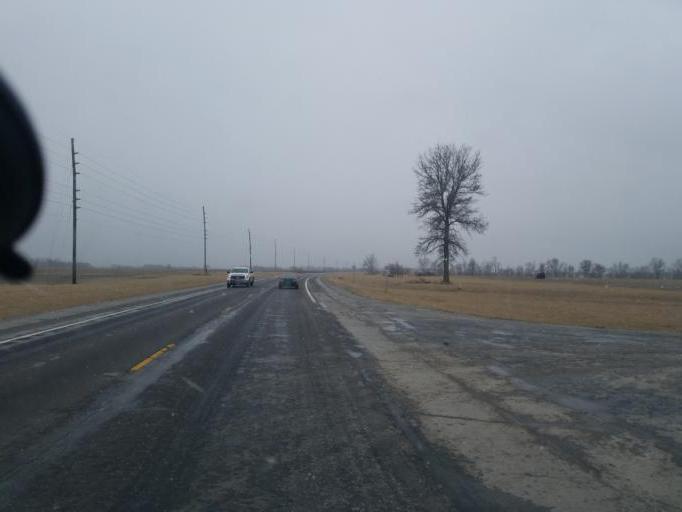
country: US
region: Missouri
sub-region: Schuyler County
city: Lancaster
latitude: 40.3769
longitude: -92.5589
